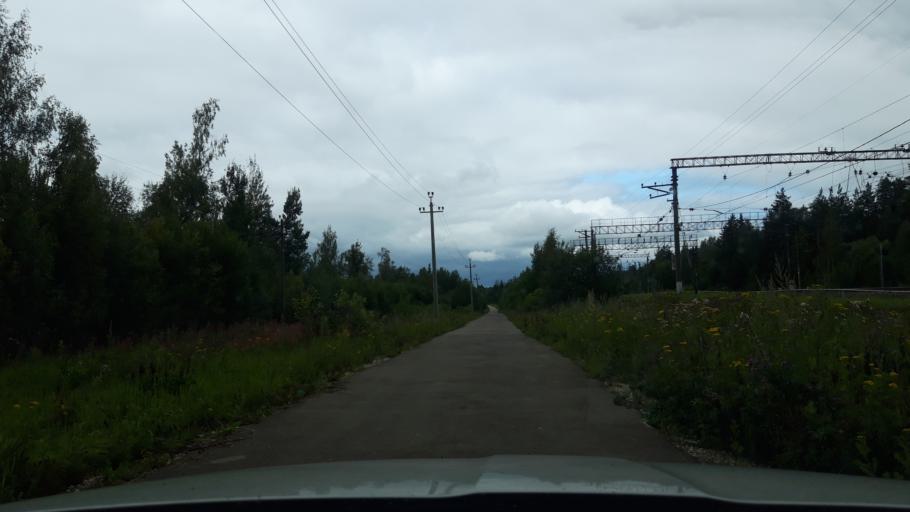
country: RU
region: Moskovskaya
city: Povarovo
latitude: 56.0398
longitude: 37.0538
